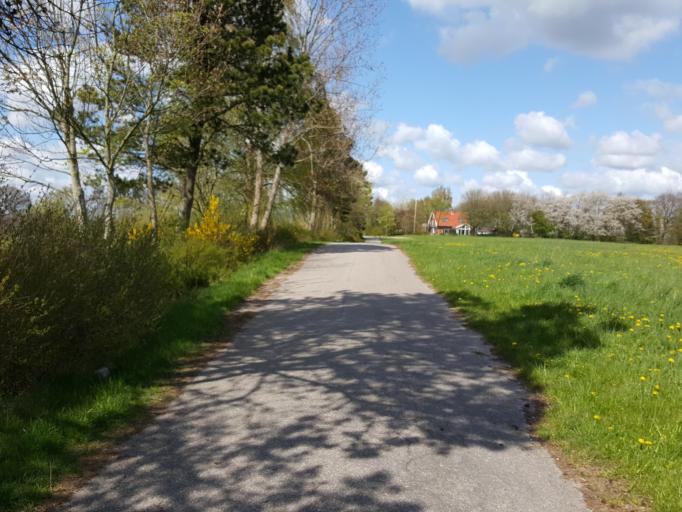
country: DK
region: Capital Region
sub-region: Rudersdal Kommune
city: Birkerod
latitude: 55.8515
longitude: 12.4590
